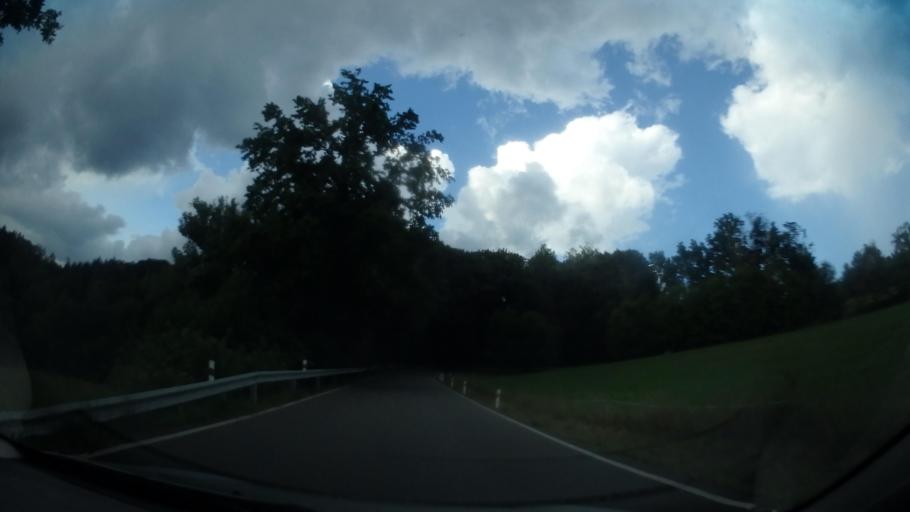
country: CZ
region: Olomoucky
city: Stity
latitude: 49.8846
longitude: 16.7899
